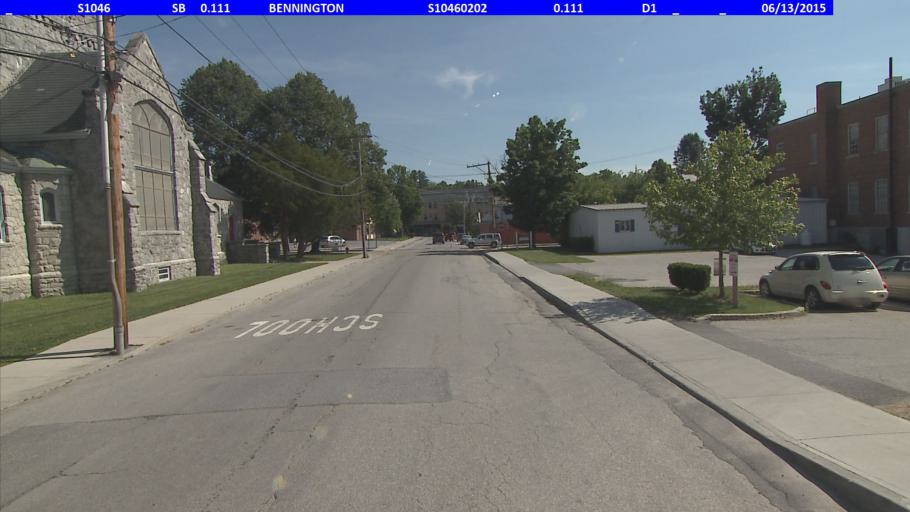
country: US
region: Vermont
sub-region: Bennington County
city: Bennington
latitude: 42.8797
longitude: -73.1950
